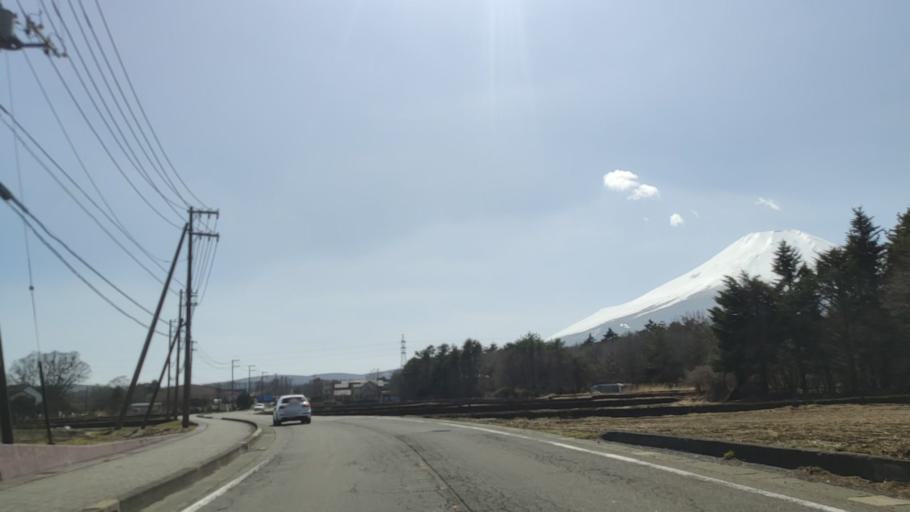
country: JP
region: Shizuoka
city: Gotemba
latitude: 35.4374
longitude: 138.8482
